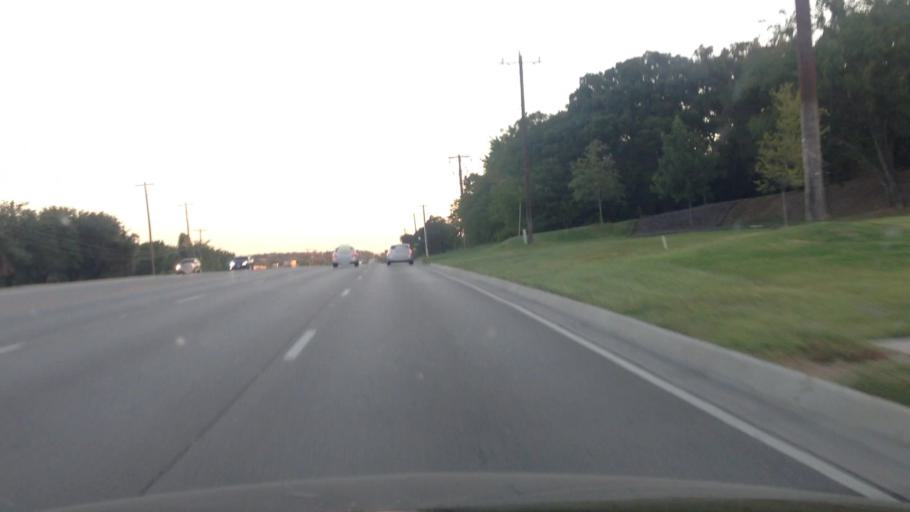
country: US
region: Texas
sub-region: Tarrant County
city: Southlake
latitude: 32.9317
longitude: -97.1858
